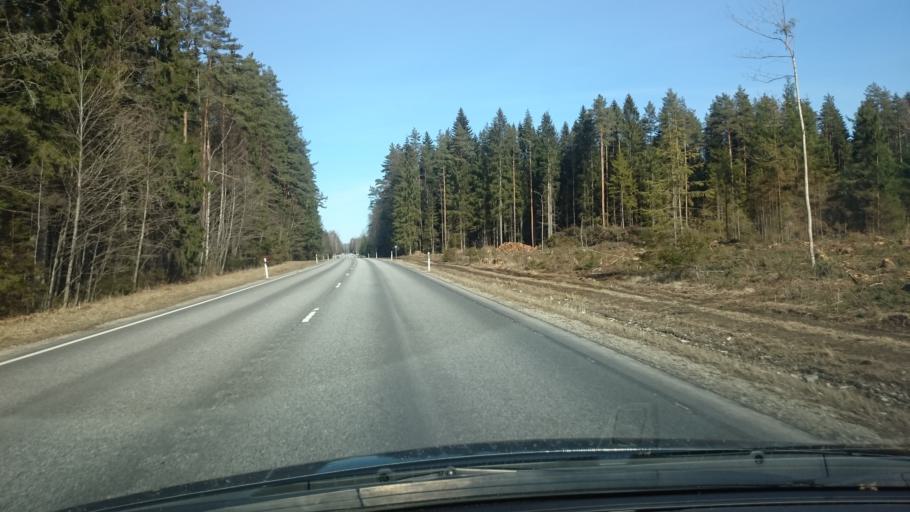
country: EE
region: Jaervamaa
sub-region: Tueri vald
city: Sarevere
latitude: 58.7014
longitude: 25.2608
